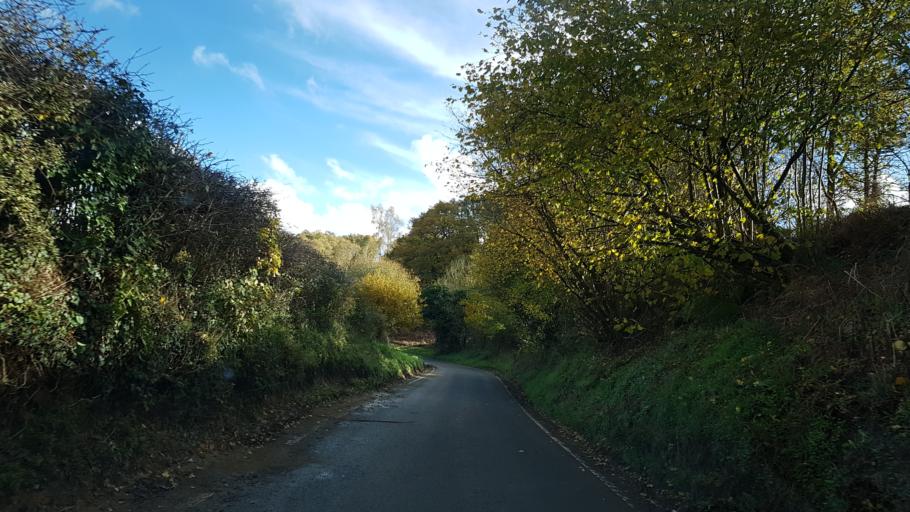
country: GB
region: England
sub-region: Surrey
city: Seale
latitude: 51.2215
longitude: -0.6875
